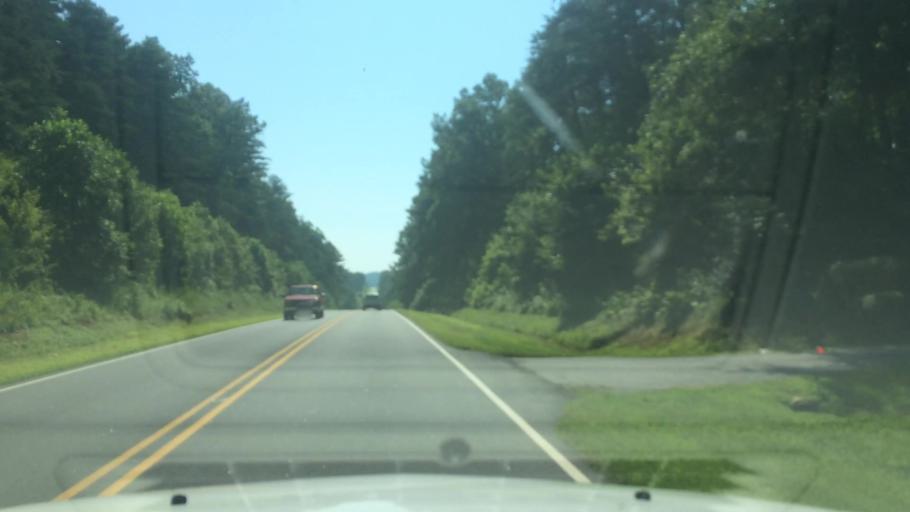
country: US
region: North Carolina
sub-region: Caldwell County
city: Hudson
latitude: 35.9088
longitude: -81.4202
